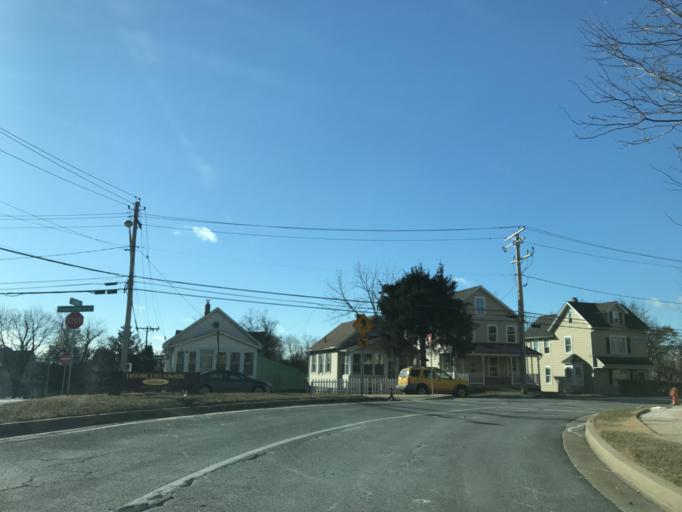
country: US
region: Maryland
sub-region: Baltimore County
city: Towson
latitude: 39.4003
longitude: -76.5967
